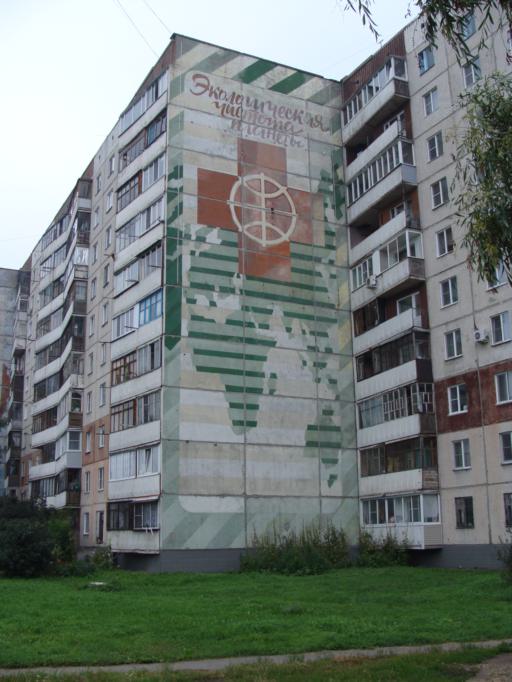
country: RU
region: Altai Krai
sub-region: Gorod Barnaulskiy
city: Barnaul
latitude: 53.3692
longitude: 83.7034
